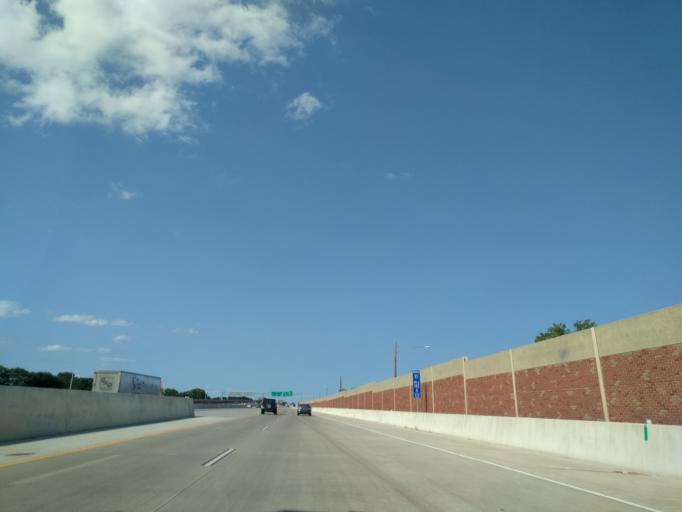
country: US
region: Wisconsin
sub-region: Brown County
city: Ashwaubenon
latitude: 44.4890
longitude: -88.0805
